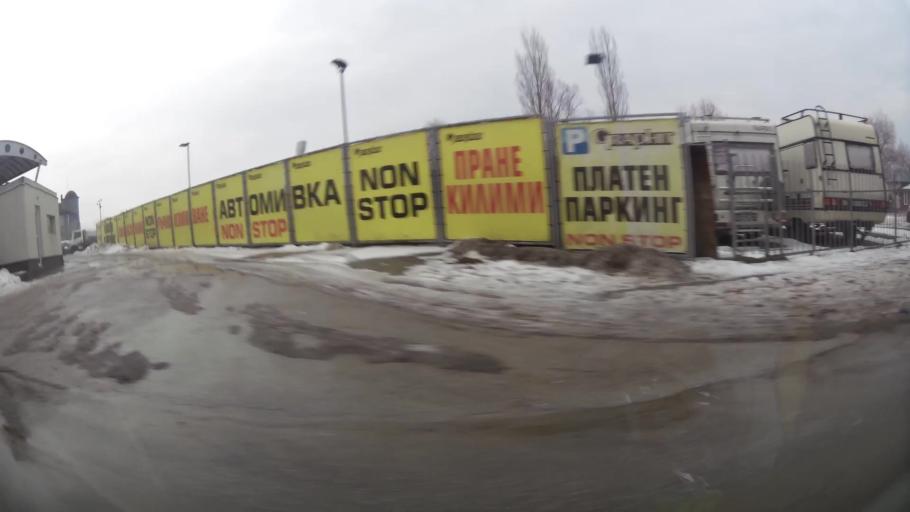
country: BG
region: Sofia-Capital
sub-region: Stolichna Obshtina
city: Sofia
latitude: 42.6899
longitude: 23.2500
